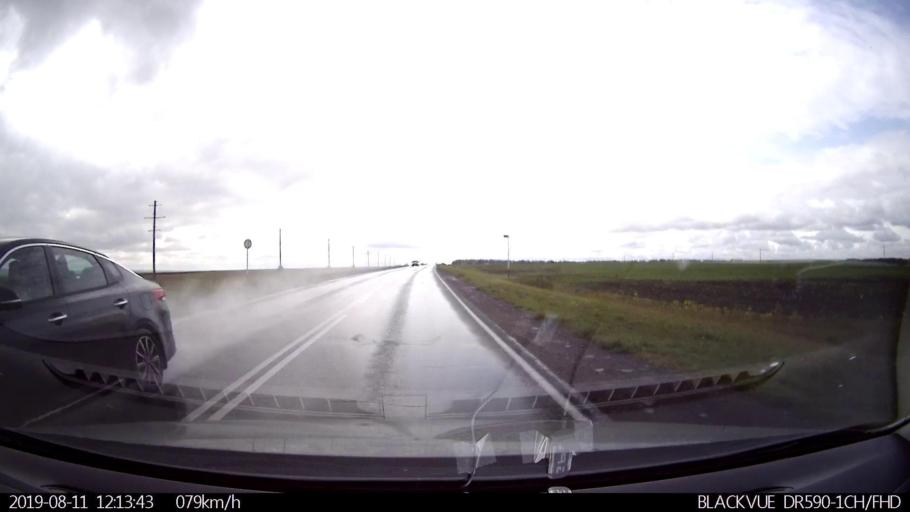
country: RU
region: Ulyanovsk
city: Ignatovka
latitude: 53.9591
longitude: 47.9894
